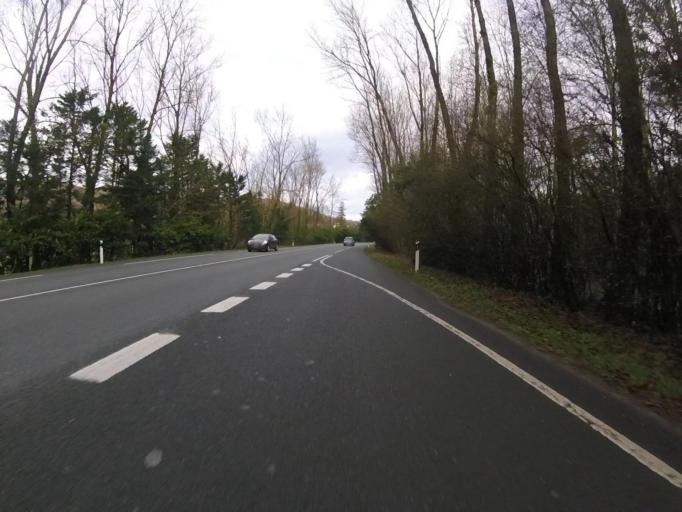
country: ES
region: Basque Country
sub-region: Provincia de Guipuzcoa
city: Irun
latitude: 43.3387
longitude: -1.8217
